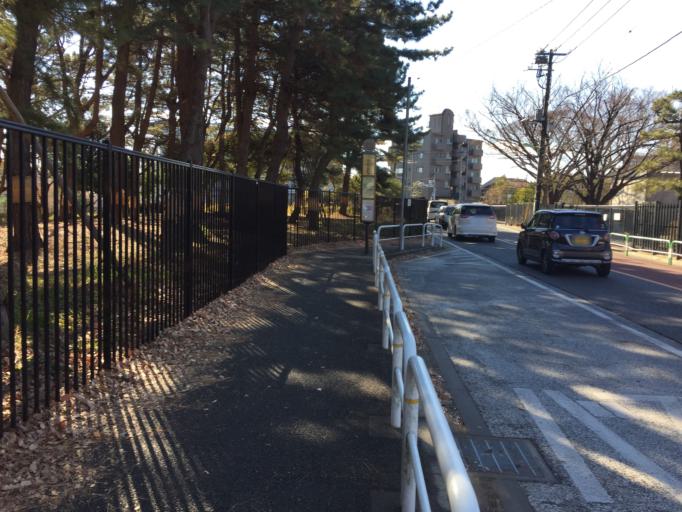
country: JP
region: Tokyo
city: Chofugaoka
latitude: 35.6293
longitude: 139.6147
